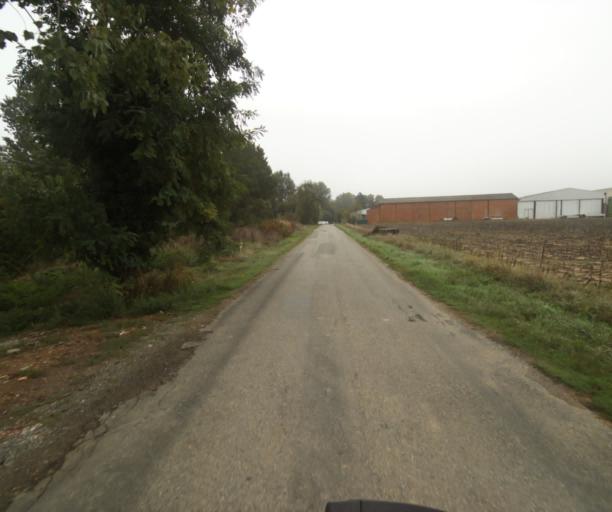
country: FR
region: Midi-Pyrenees
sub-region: Departement du Tarn-et-Garonne
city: Nohic
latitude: 43.9071
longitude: 1.4382
